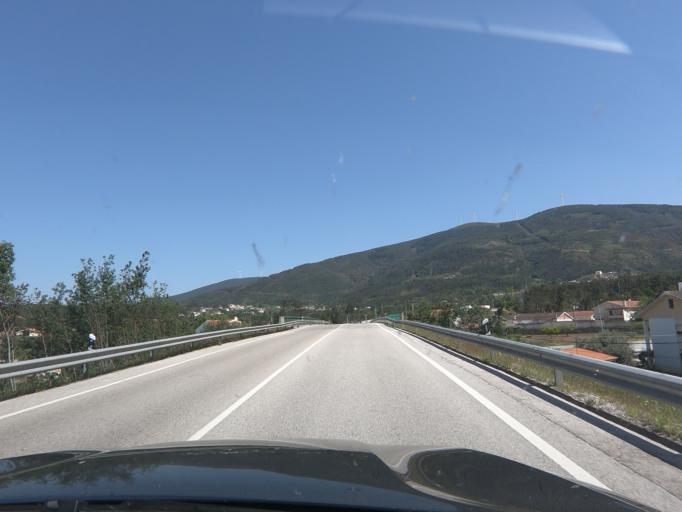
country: PT
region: Coimbra
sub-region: Lousa
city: Lousa
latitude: 40.1271
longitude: -8.2401
